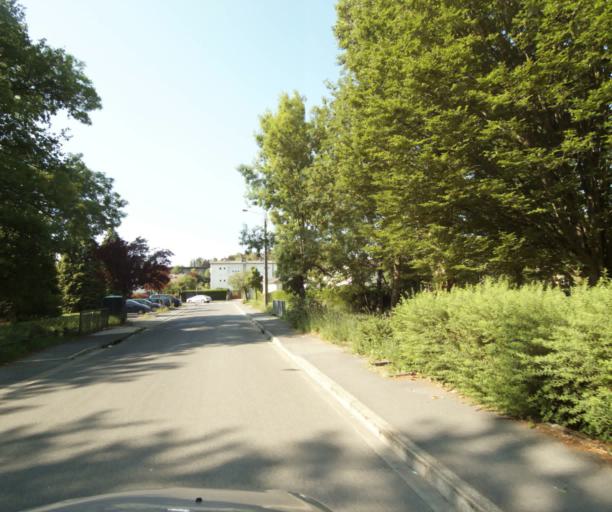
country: FR
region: Champagne-Ardenne
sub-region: Departement des Ardennes
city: Charleville-Mezieres
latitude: 49.7825
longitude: 4.7033
